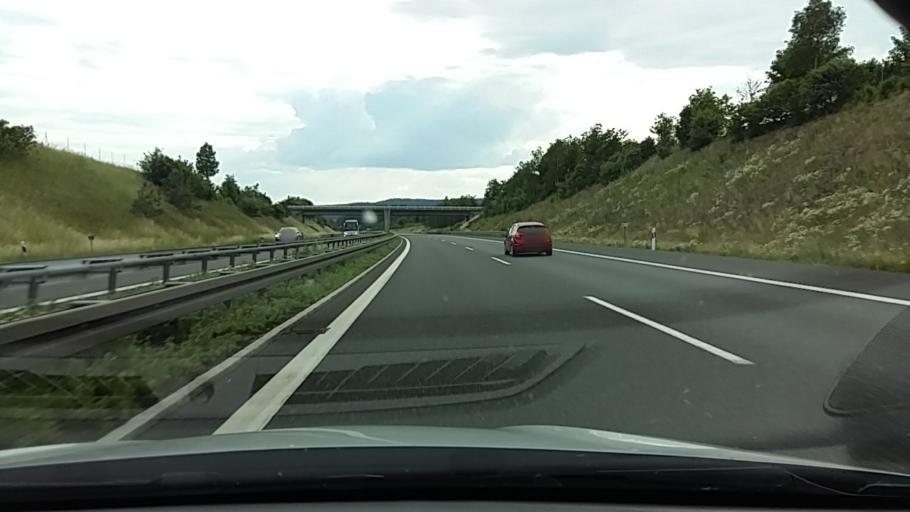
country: DE
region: Bavaria
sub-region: Upper Palatinate
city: Leuchtenberg
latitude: 49.5685
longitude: 12.2203
